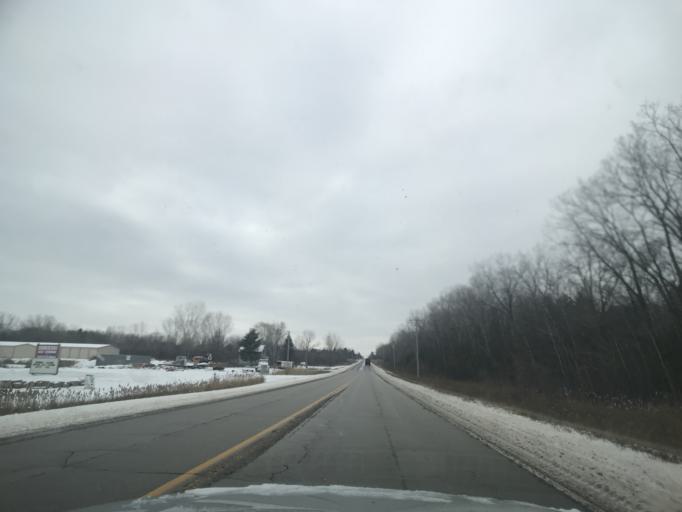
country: US
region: Wisconsin
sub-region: Brown County
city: Suamico
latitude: 44.7210
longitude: -88.0560
